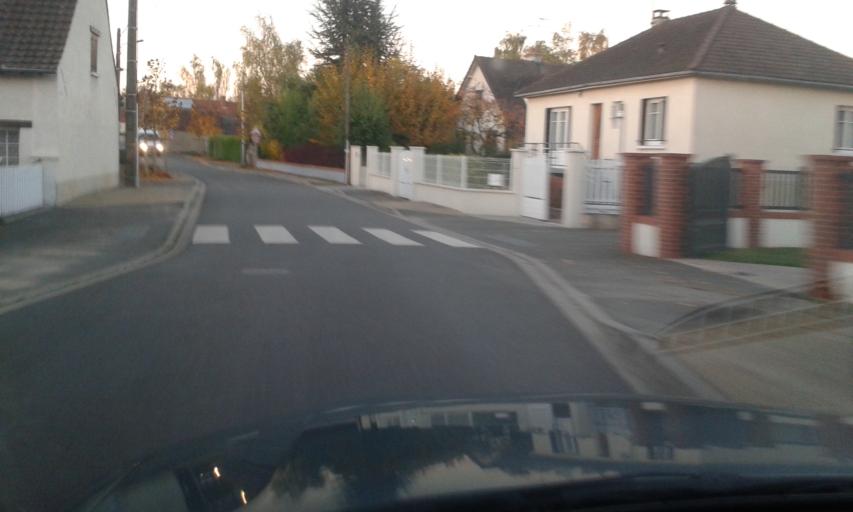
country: FR
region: Centre
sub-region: Departement du Loiret
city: Olivet
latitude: 47.8530
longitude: 1.8824
